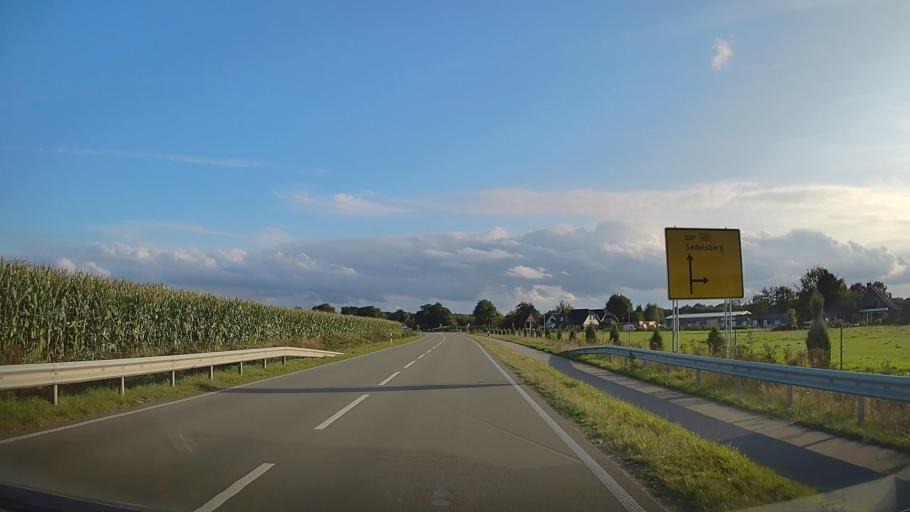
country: DE
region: Lower Saxony
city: Hilkenbrook
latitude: 53.0662
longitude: 7.7225
